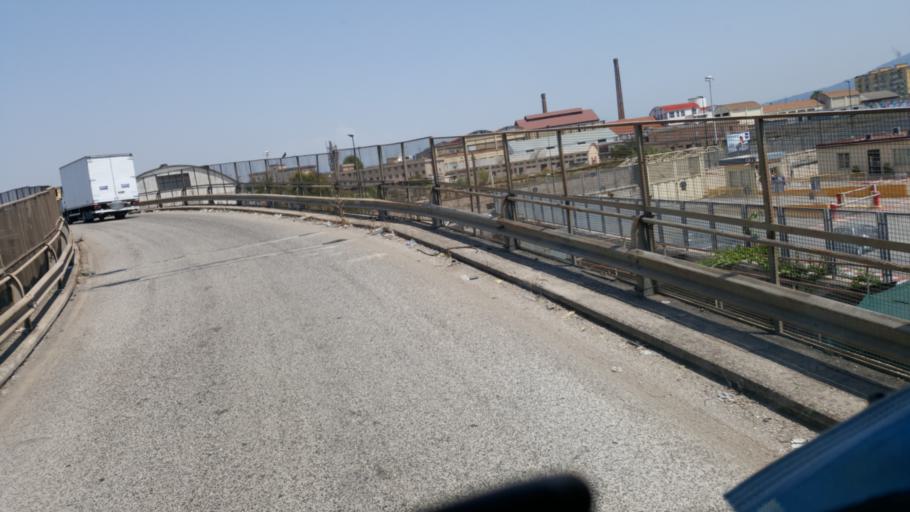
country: IT
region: Campania
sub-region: Provincia di Napoli
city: San Giorgio a Cremano
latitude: 40.8465
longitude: 14.2968
